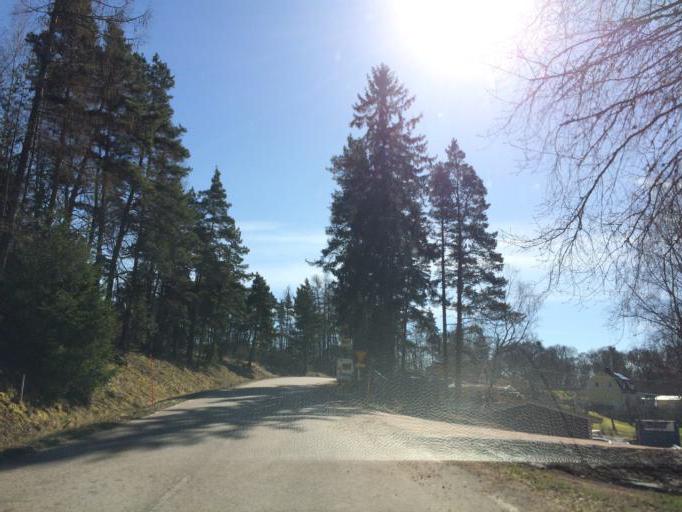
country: SE
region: Soedermanland
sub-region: Eskilstuna Kommun
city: Kvicksund
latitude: 59.5030
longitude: 16.2797
